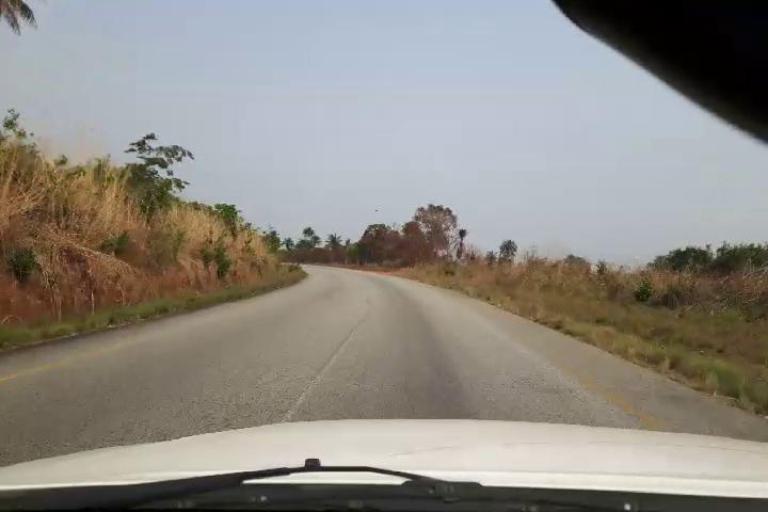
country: SL
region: Southern Province
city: Largo
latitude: 8.3026
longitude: -12.2002
